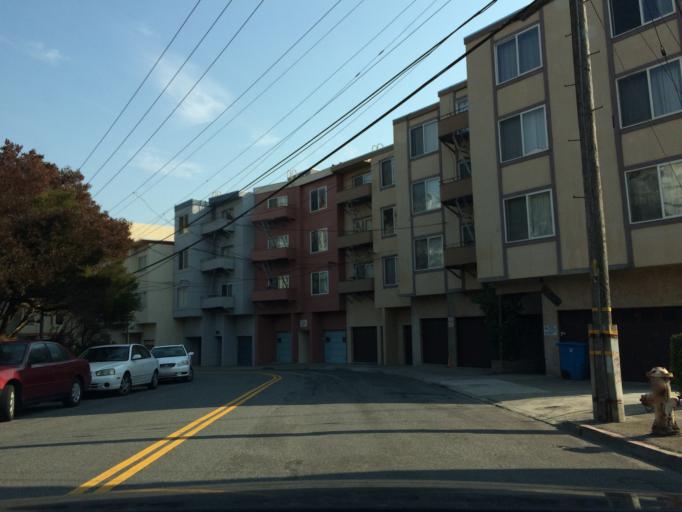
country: US
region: California
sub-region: San Francisco County
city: San Francisco
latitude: 37.7516
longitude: -122.4444
